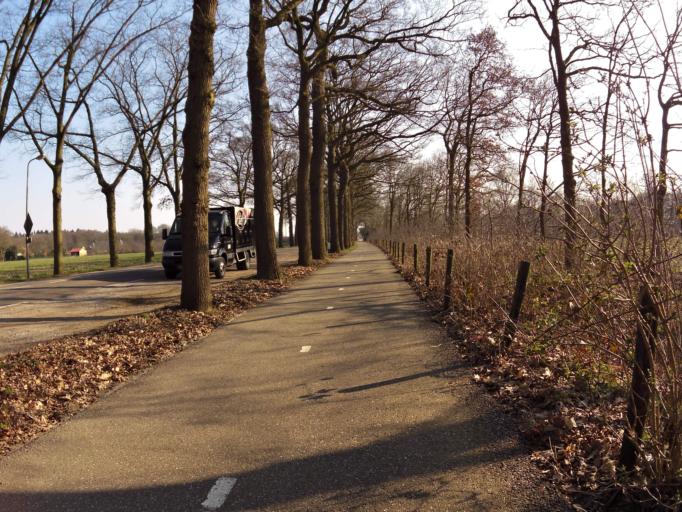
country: NL
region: North Brabant
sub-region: Gemeente Maasdonk
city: Geffen
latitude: 51.7188
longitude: 5.4008
